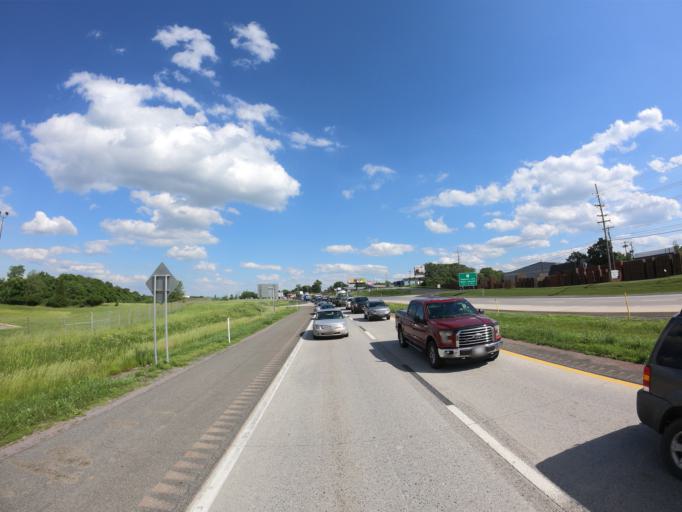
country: US
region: West Virginia
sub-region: Berkeley County
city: Martinsburg
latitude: 39.4340
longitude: -77.9573
